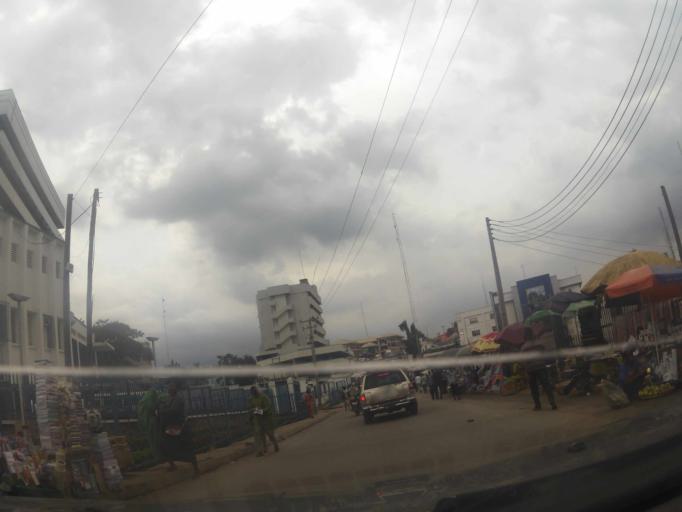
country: NG
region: Oyo
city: Ibadan
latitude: 7.3890
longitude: 3.8804
